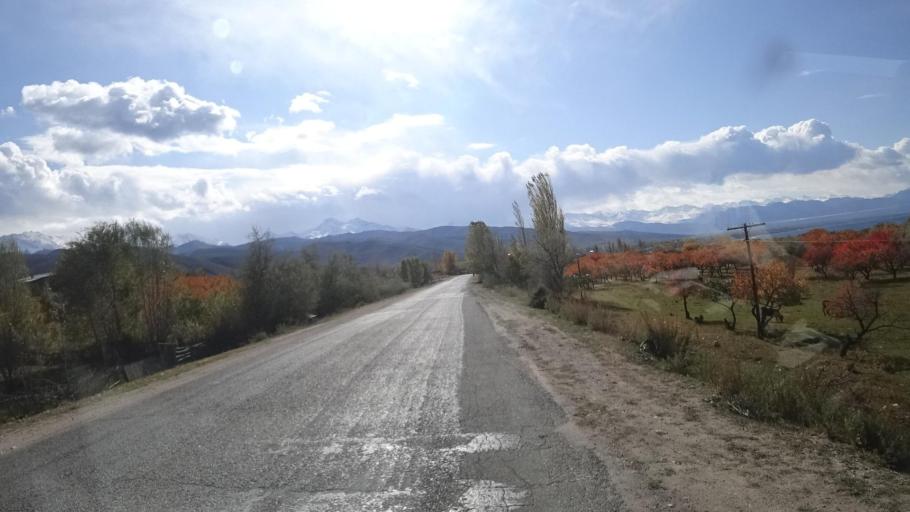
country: KG
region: Ysyk-Koel
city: Pokrovka
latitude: 42.2289
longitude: 77.7147
